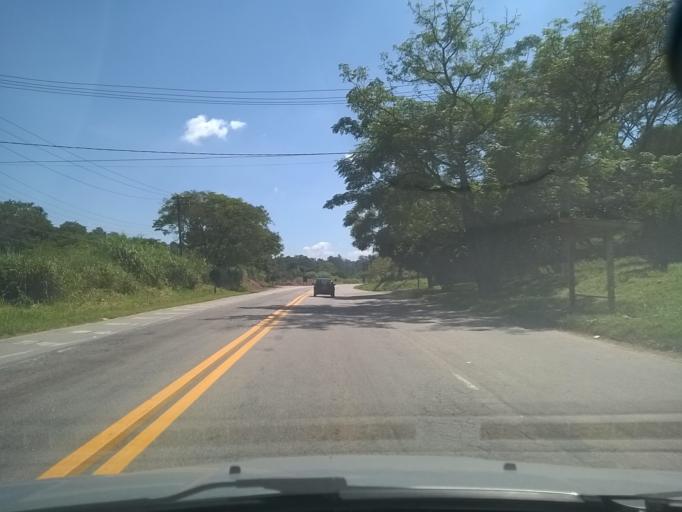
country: BR
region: Sao Paulo
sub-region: Varzea Paulista
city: Varzea Paulista
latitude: -23.2388
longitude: -46.8560
